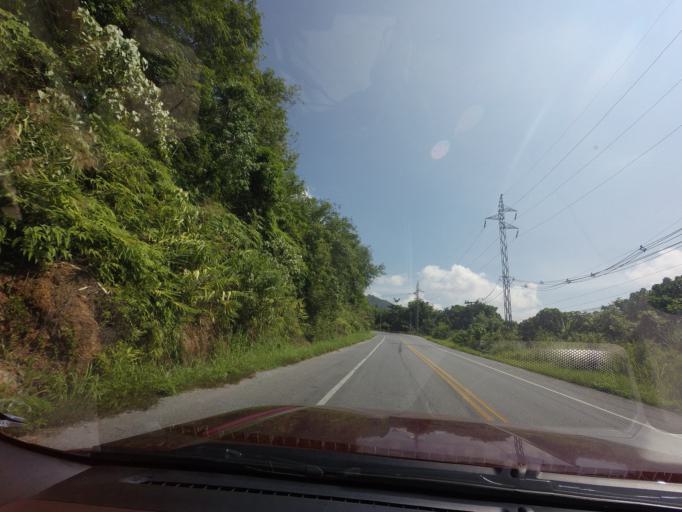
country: TH
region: Yala
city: Betong
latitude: 5.8576
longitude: 101.1201
